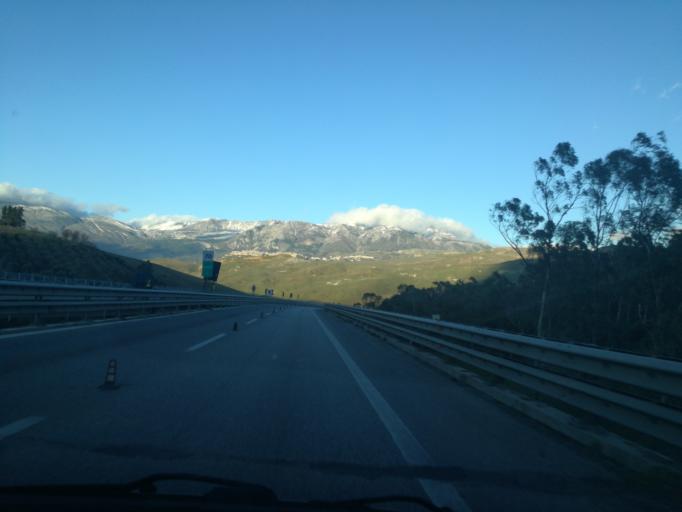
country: IT
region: Sicily
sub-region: Palermo
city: Polizzi Generosa
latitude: 37.7644
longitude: 13.9675
